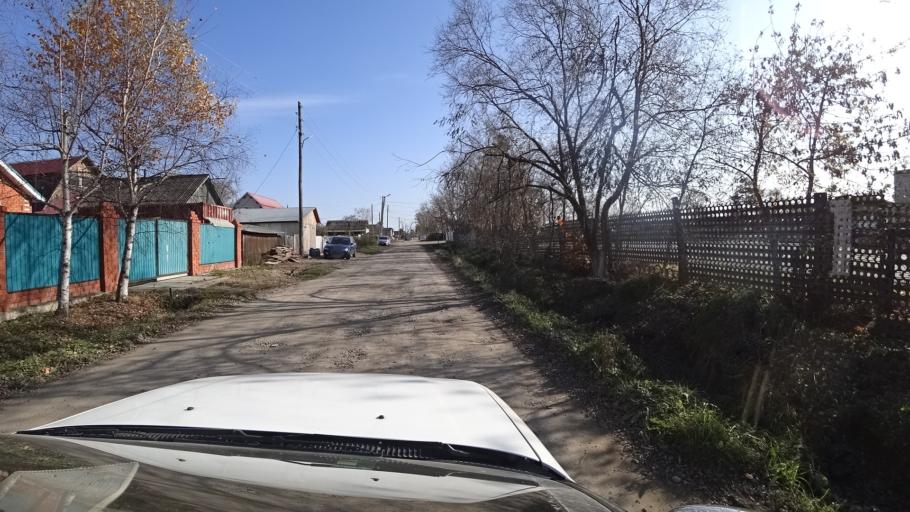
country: RU
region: Primorskiy
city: Dal'nerechensk
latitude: 45.9257
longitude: 133.7315
